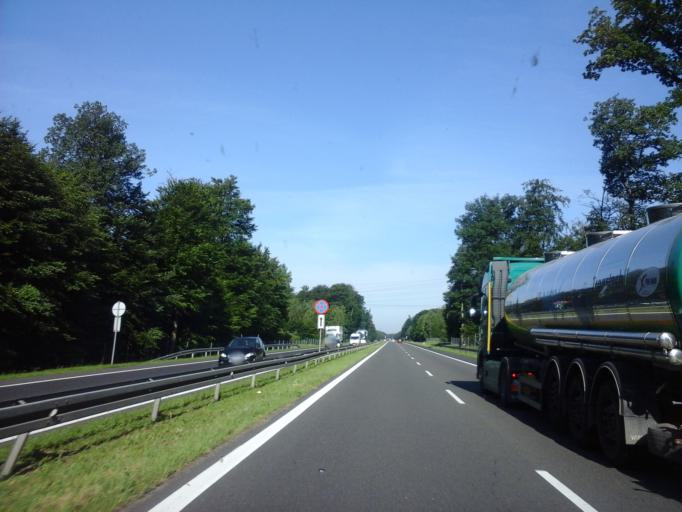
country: PL
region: West Pomeranian Voivodeship
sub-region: Powiat stargardzki
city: Kobylanka
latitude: 53.3545
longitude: 14.8025
